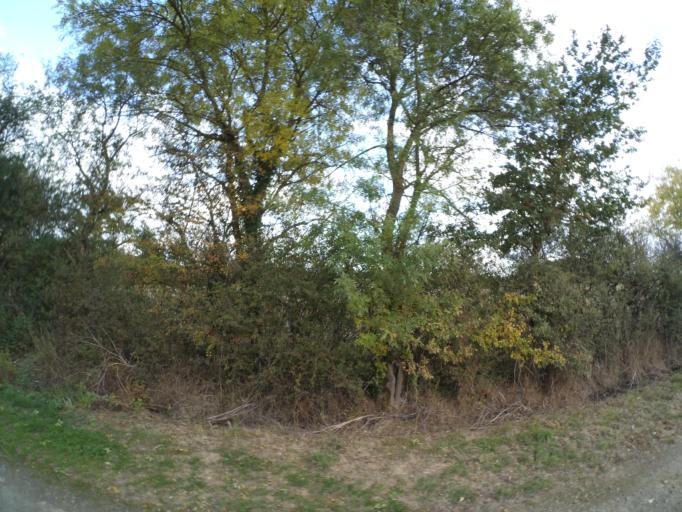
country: FR
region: Pays de la Loire
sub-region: Departement de la Loire-Atlantique
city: Saint-Lumine-de-Clisson
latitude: 47.0782
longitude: -1.3358
